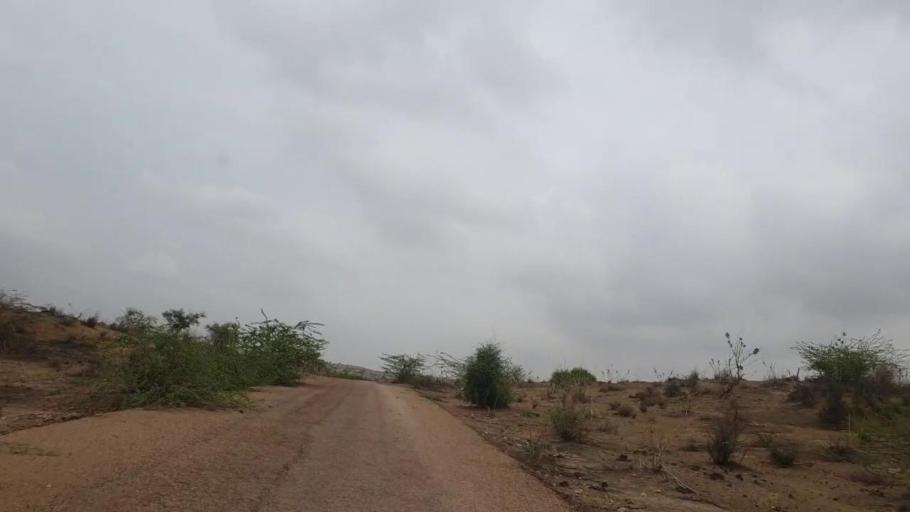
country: PK
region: Sindh
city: Diplo
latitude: 24.5206
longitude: 69.4695
